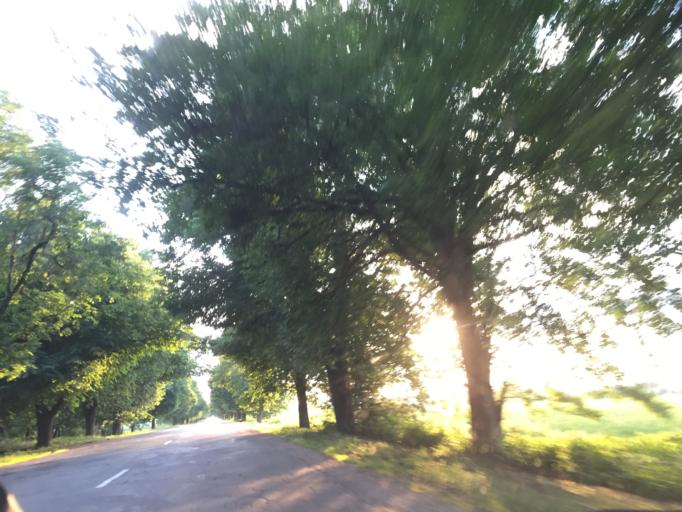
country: LV
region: Sigulda
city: Sigulda
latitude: 57.1388
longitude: 24.8813
